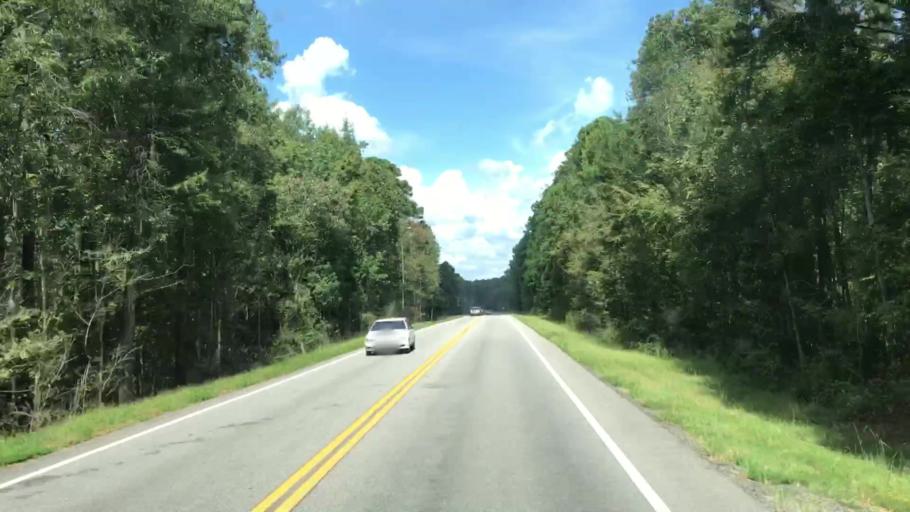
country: US
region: Georgia
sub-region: Greene County
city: Greensboro
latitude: 33.6276
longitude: -83.2146
